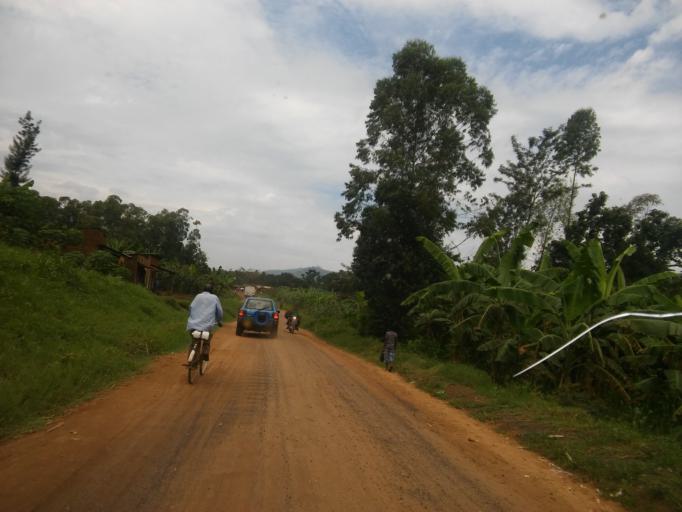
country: UG
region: Eastern Region
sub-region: Bududa District
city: Bududa
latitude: 0.9371
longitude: 34.2828
